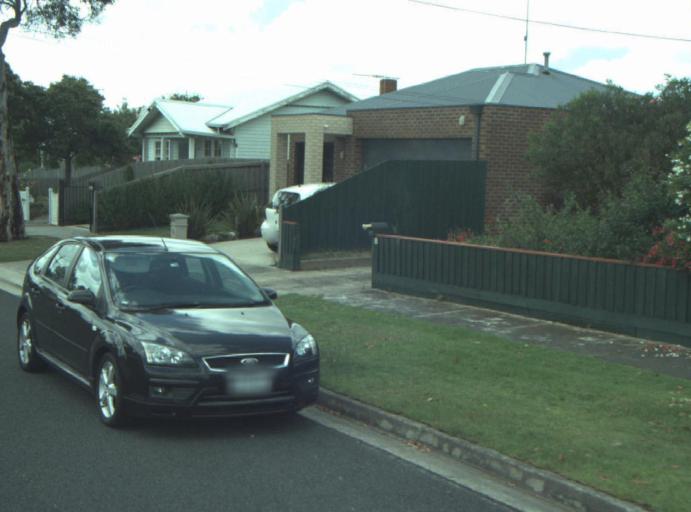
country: AU
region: Victoria
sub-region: Greater Geelong
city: Breakwater
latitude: -38.1752
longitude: 144.3502
